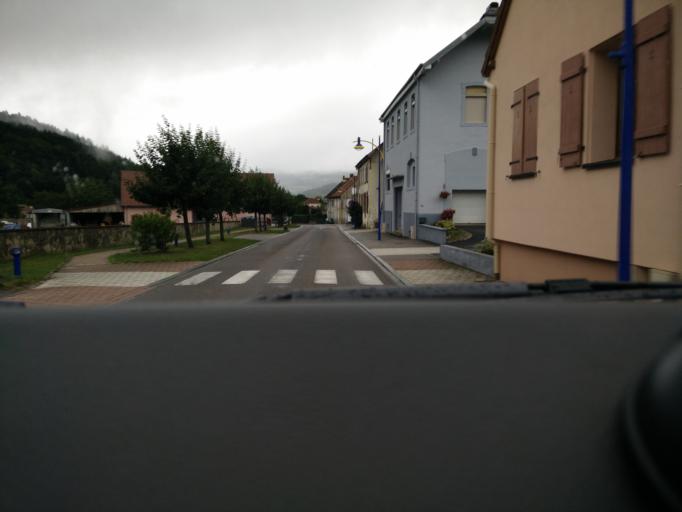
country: FR
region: Lorraine
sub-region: Departement des Vosges
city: Plainfaing
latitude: 48.1627
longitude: 7.0092
